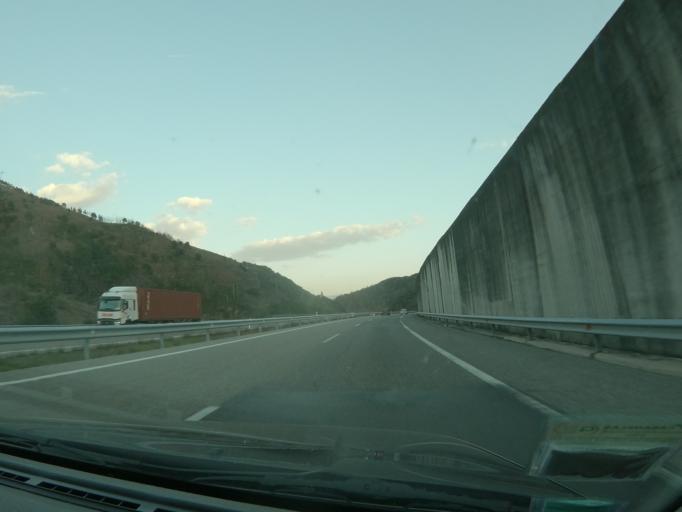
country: ES
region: Castille and Leon
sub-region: Provincia de Leon
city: Villafranca del Bierzo
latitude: 42.6203
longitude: -6.8328
